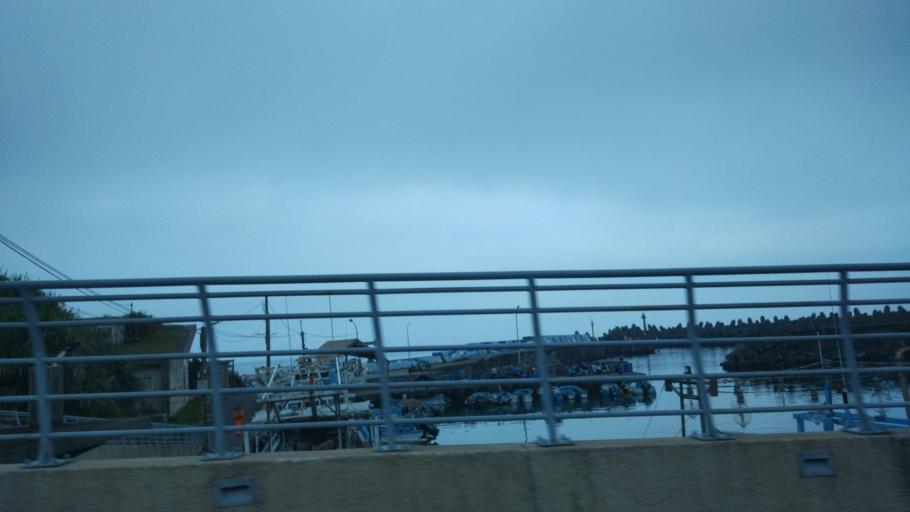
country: TW
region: Taiwan
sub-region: Keelung
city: Keelung
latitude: 25.2038
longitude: 121.6913
